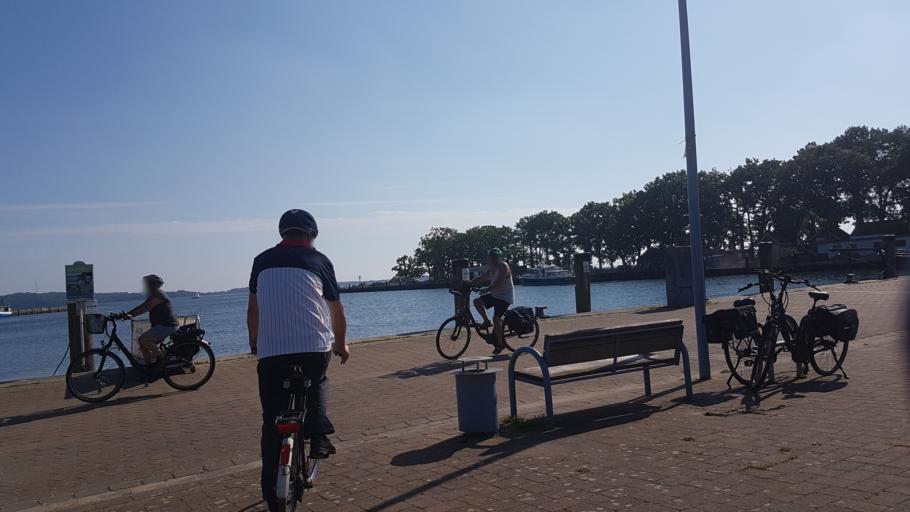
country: DE
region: Mecklenburg-Vorpommern
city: Putbus
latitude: 54.3424
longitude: 13.5002
